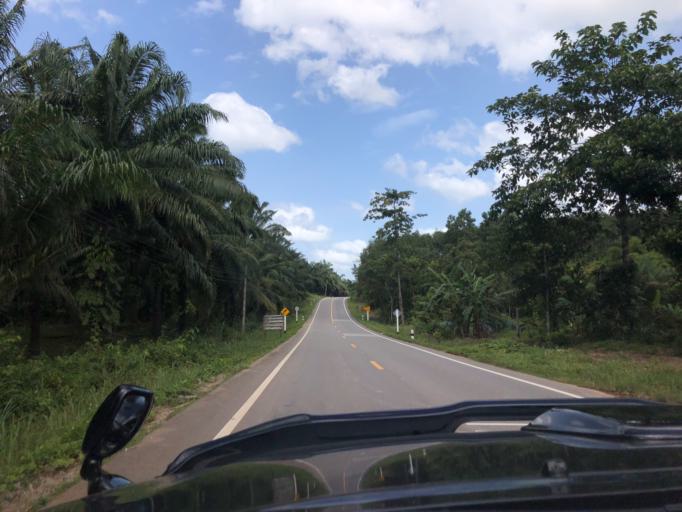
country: TH
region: Krabi
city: Khlong Thom
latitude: 7.9482
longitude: 99.2072
